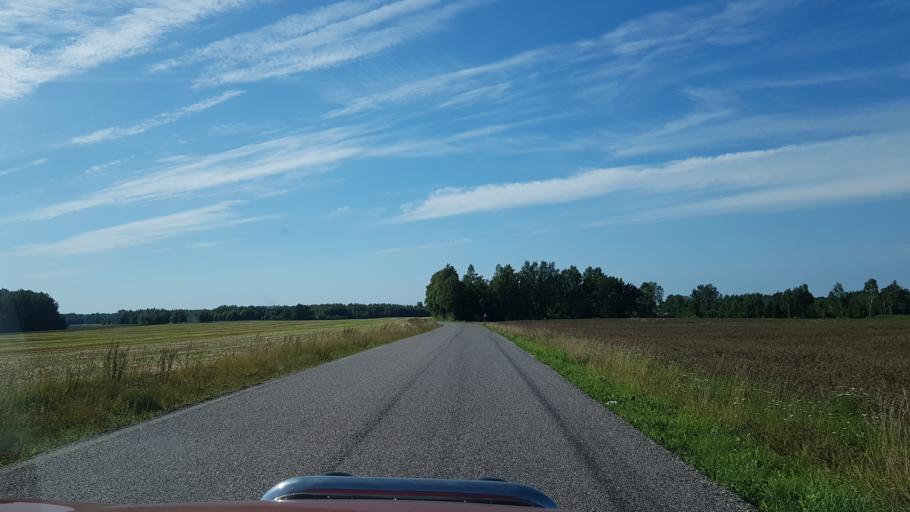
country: EE
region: Tartu
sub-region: Puhja vald
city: Puhja
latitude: 58.2555
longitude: 26.2874
